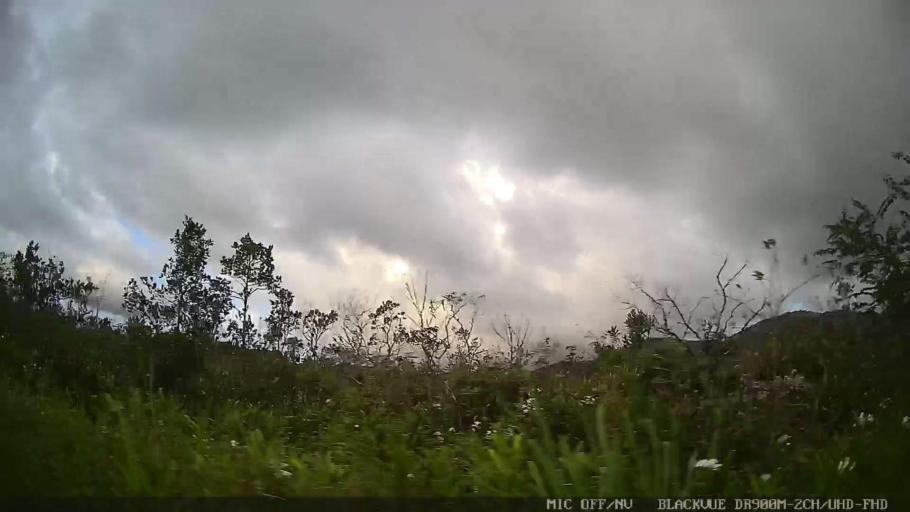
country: BR
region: Sao Paulo
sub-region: Itanhaem
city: Itanhaem
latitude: -24.1327
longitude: -46.7792
